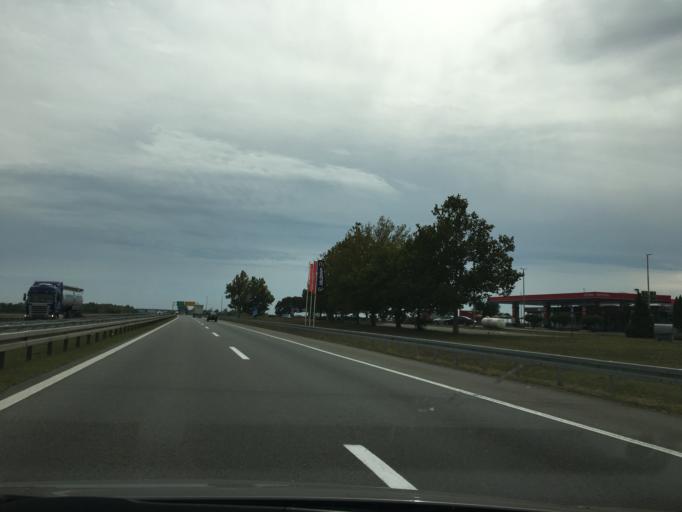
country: RS
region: Autonomna Pokrajina Vojvodina
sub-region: Sremski Okrug
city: Stara Pazova
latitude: 44.9956
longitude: 20.2079
